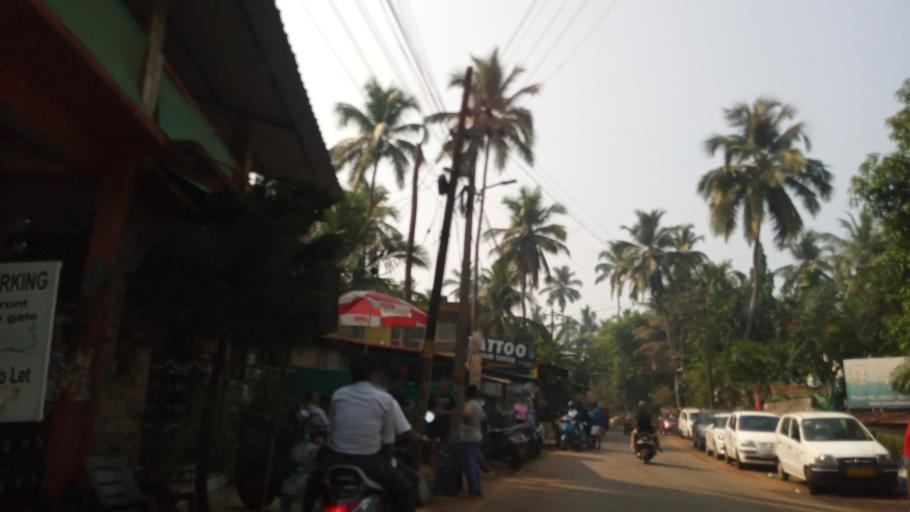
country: IN
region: Goa
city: Calangute
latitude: 15.5401
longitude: 73.7609
